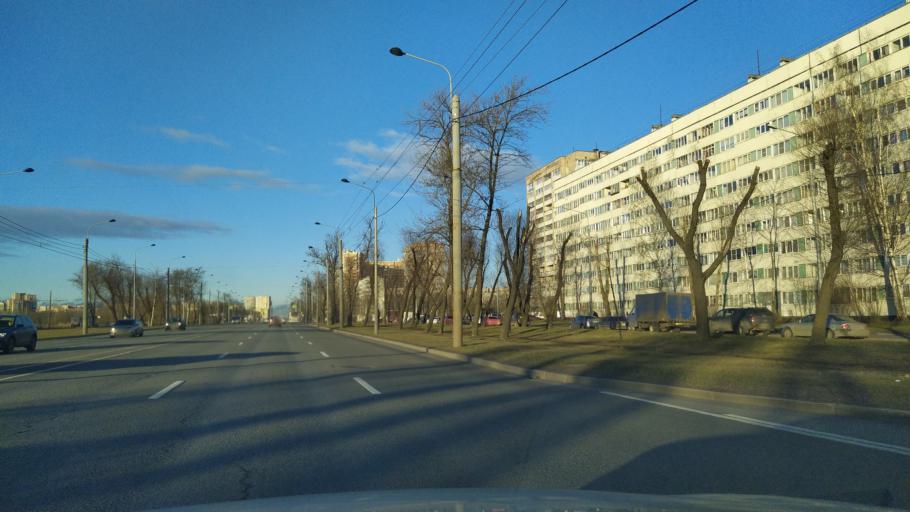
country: RU
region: St.-Petersburg
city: Uritsk
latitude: 59.8370
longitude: 30.2001
